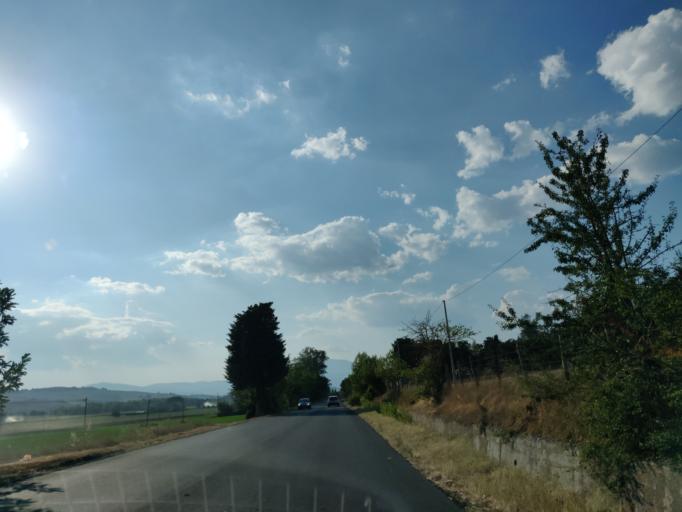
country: IT
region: Latium
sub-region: Provincia di Viterbo
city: Proceno
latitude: 42.7760
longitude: 11.8436
